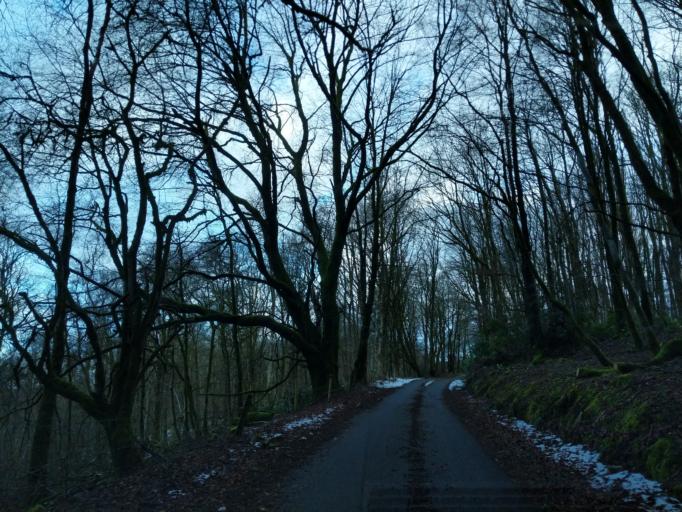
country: GB
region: Scotland
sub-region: Dumfries and Galloway
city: Moffat
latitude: 55.3236
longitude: -3.4755
